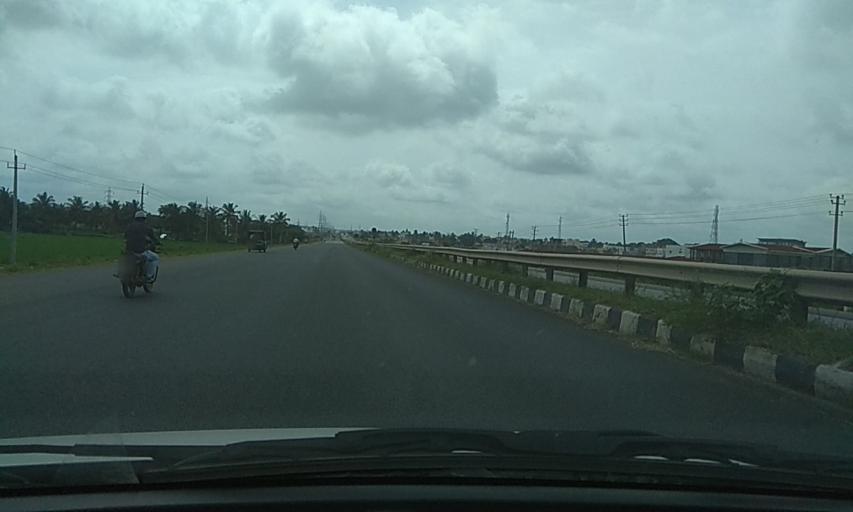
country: IN
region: Karnataka
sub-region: Davanagere
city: Harihar
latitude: 14.4453
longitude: 75.8901
